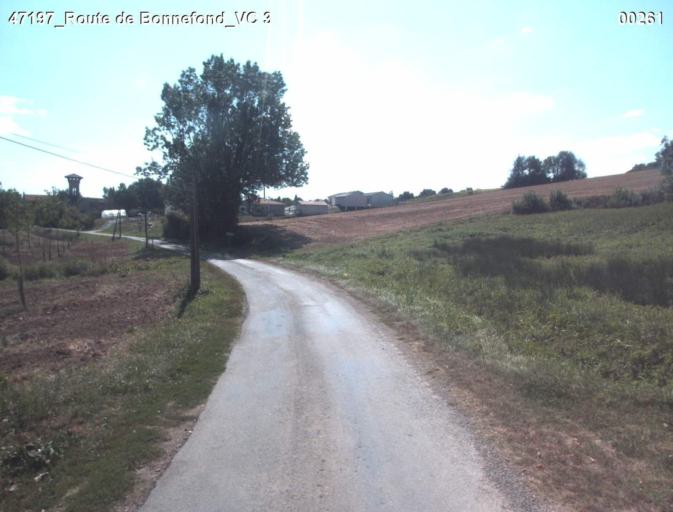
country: FR
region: Aquitaine
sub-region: Departement du Lot-et-Garonne
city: Laplume
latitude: 44.0977
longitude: 0.4751
